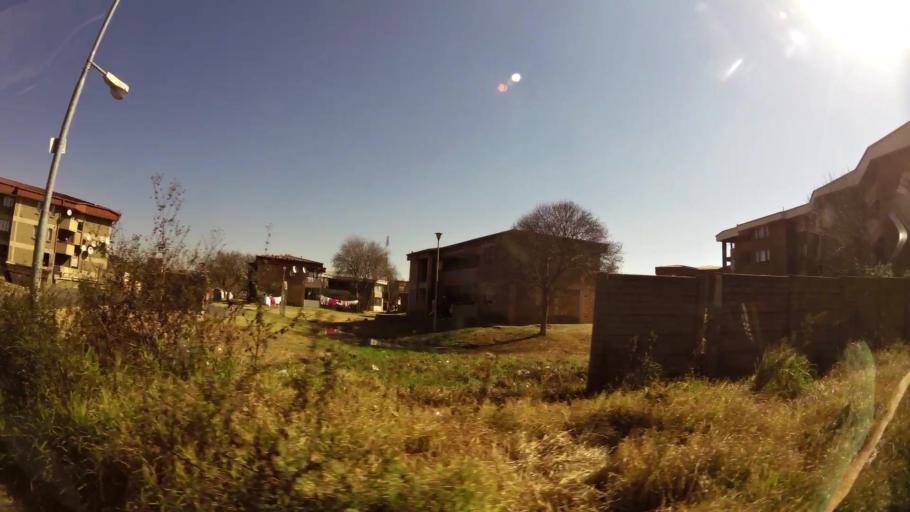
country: ZA
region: Gauteng
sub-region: City of Johannesburg Metropolitan Municipality
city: Johannesburg
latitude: -26.1788
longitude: 27.9694
